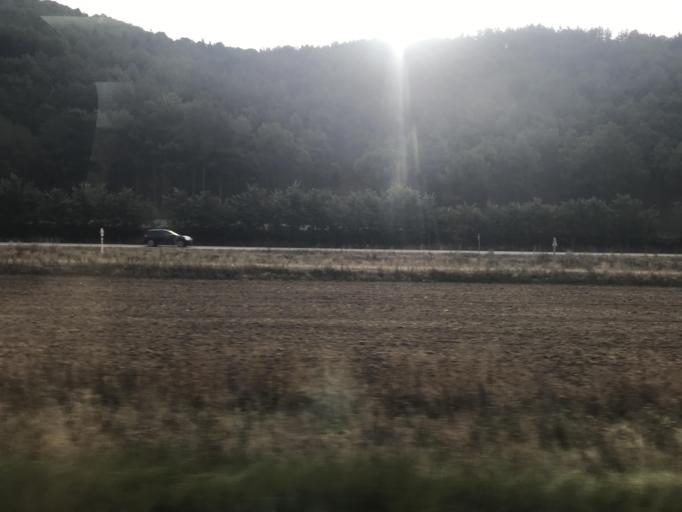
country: ES
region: Castille and Leon
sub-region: Provincia de Burgos
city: Pradanos de Bureba
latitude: 42.5198
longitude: -3.3355
